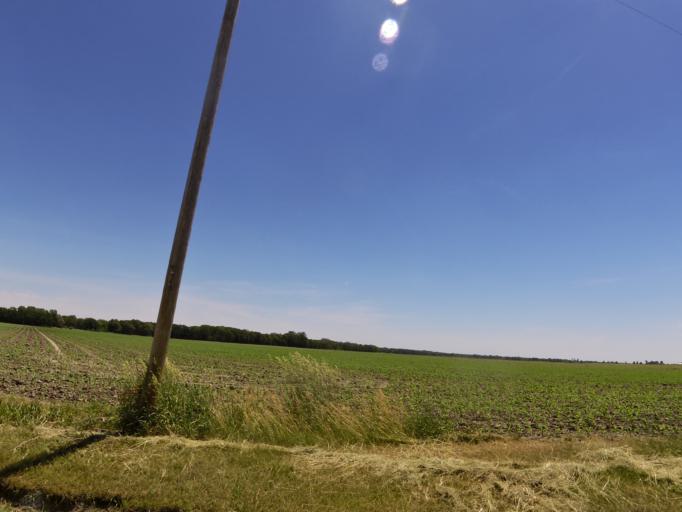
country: US
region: Illinois
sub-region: Iroquois County
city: Milford
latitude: 40.6843
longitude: -87.7548
